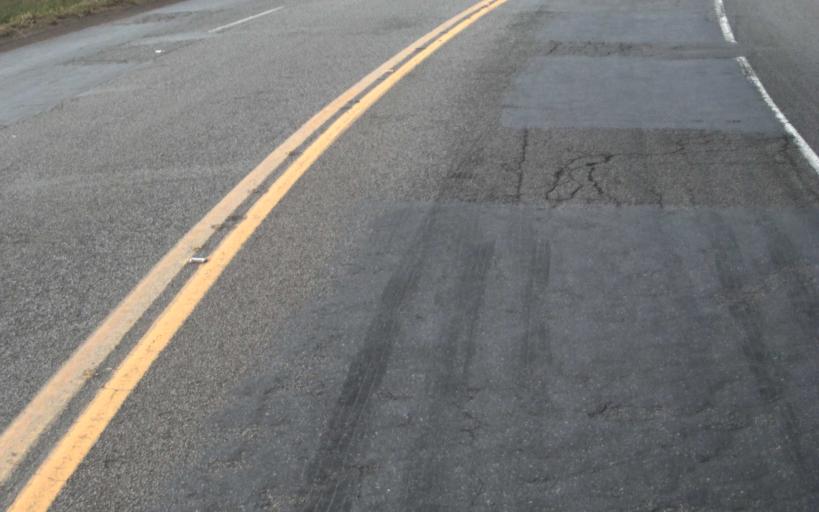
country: BR
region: Minas Gerais
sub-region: Caete
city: Caete
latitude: -19.7874
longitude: -43.6918
